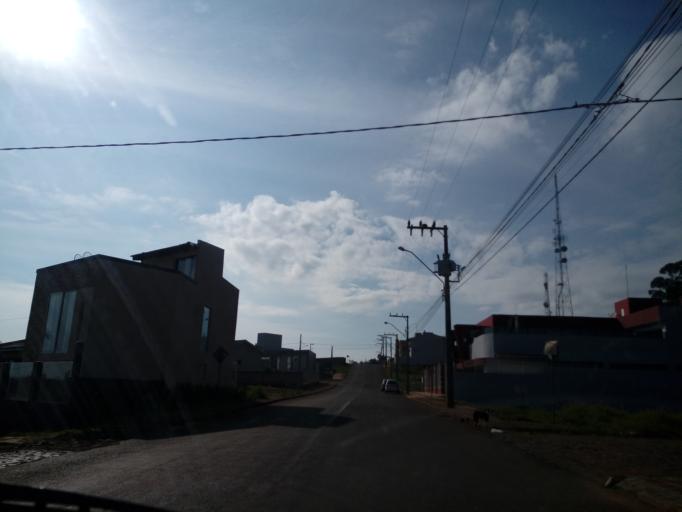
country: BR
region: Santa Catarina
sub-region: Chapeco
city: Chapeco
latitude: -27.1055
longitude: -52.5856
